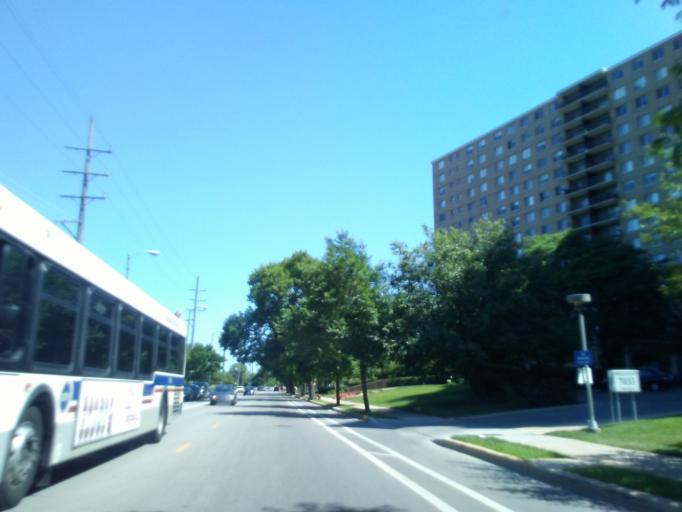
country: US
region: Illinois
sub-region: Cook County
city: Lincolnwood
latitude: 42.0085
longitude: -87.7092
